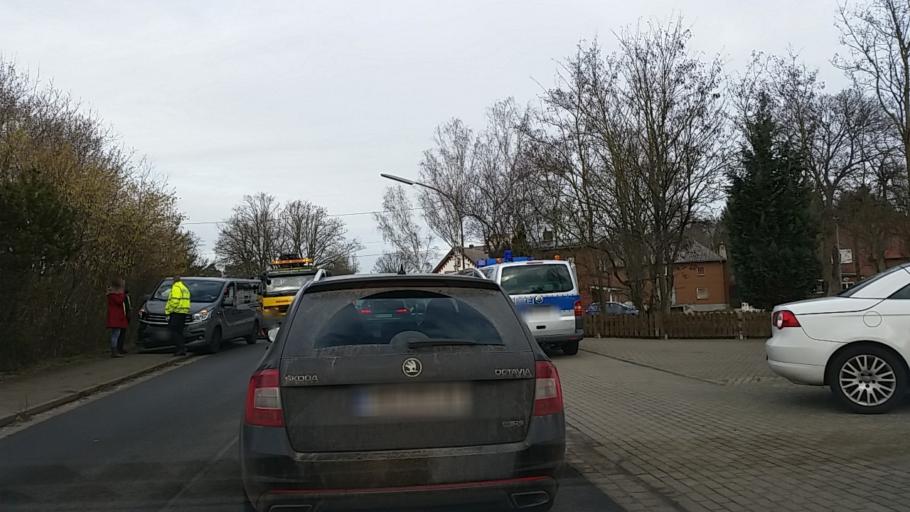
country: DE
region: Lower Saxony
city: Soltendieck
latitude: 52.8738
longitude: 10.7604
